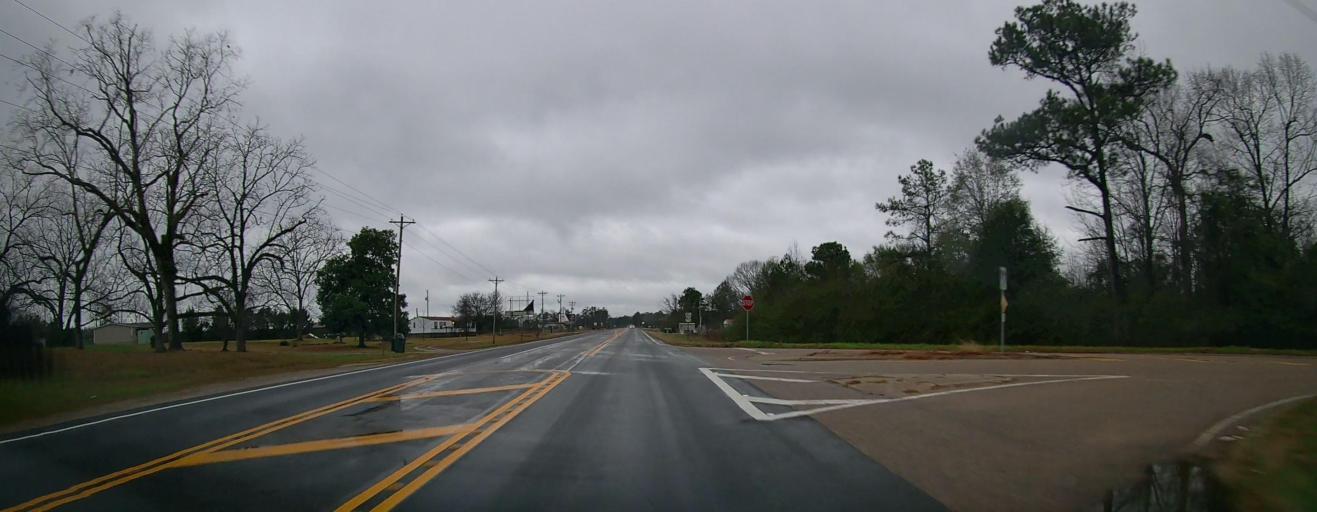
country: US
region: Alabama
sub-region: Chilton County
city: Thorsby
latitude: 32.7900
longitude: -86.9048
